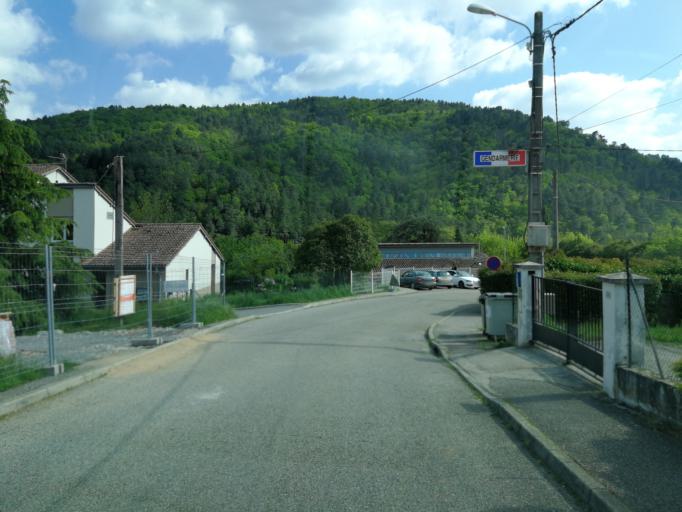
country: FR
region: Rhone-Alpes
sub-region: Departement de l'Ardeche
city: Saint-Sauveur-de-Montagut
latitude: 44.8060
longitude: 4.6221
